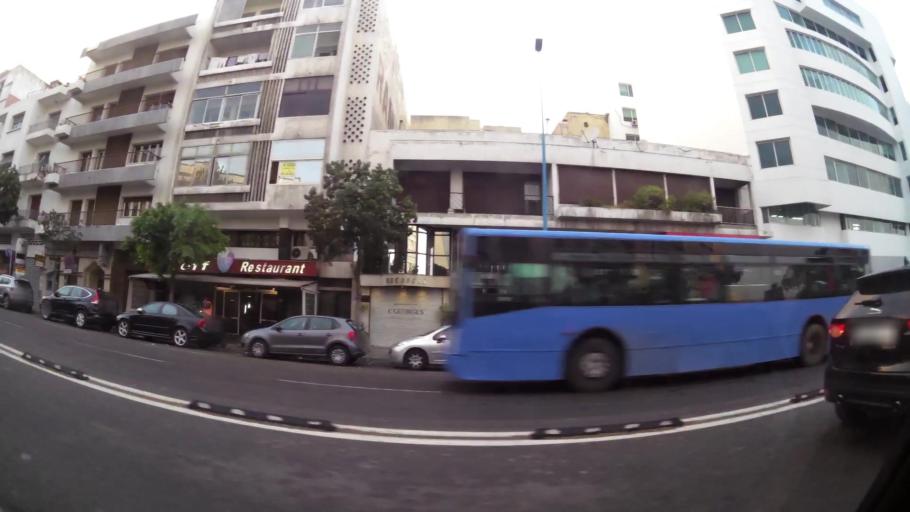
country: MA
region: Grand Casablanca
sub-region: Casablanca
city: Casablanca
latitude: 33.5852
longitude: -7.6300
